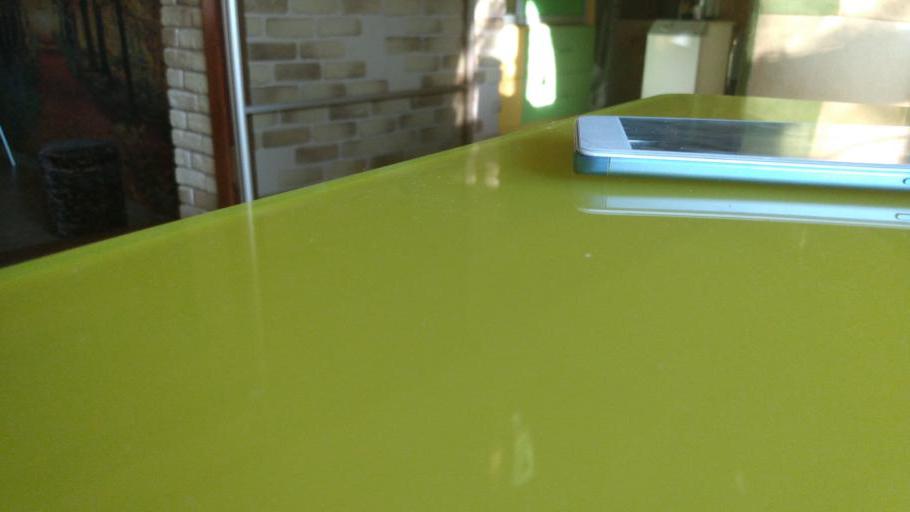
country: RU
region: Tverskaya
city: Vyshniy Volochek
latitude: 57.4503
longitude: 34.5745
